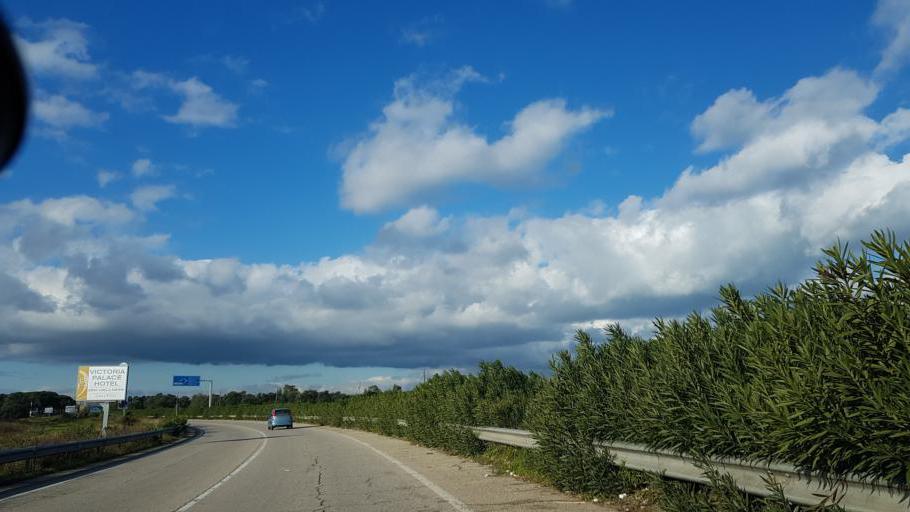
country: IT
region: Apulia
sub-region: Provincia di Brindisi
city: Materdomini
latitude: 40.6585
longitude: 17.9332
